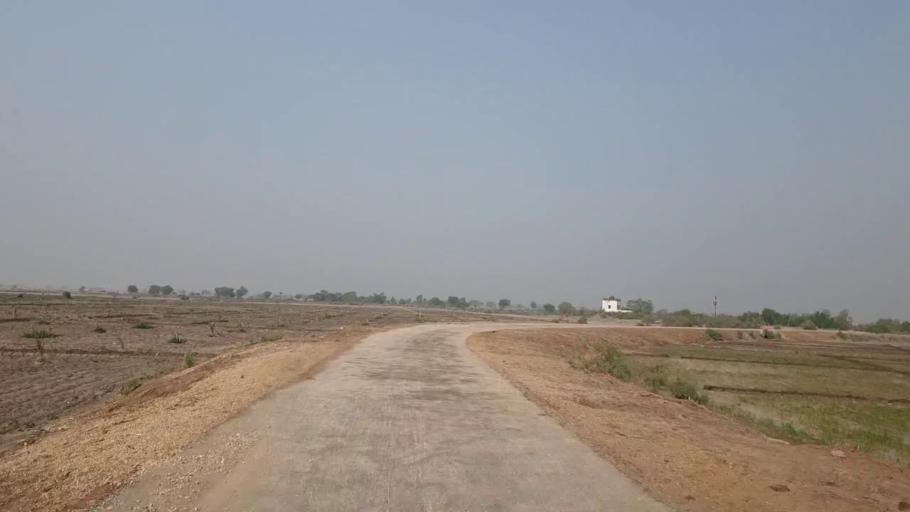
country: PK
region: Sindh
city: Bhan
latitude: 26.4869
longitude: 67.7000
